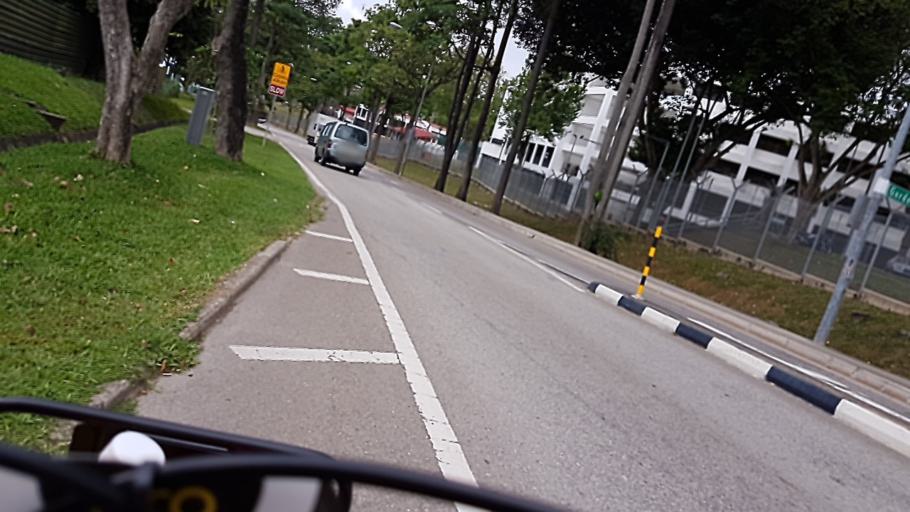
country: MY
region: Johor
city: Kampung Pasir Gudang Baru
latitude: 1.3679
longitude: 103.9772
